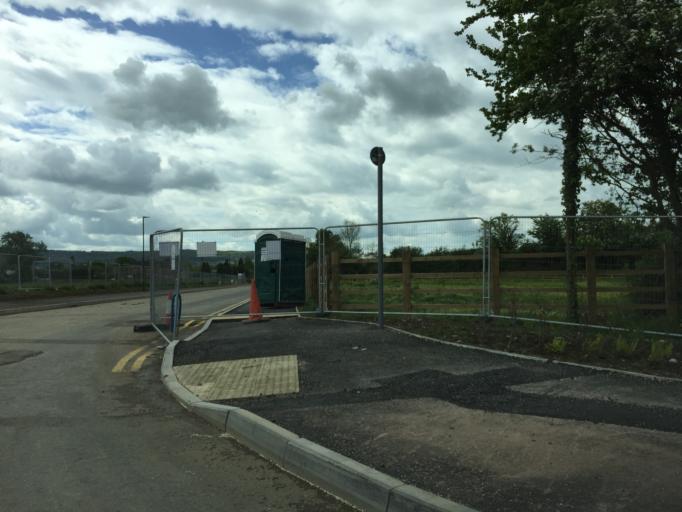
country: GB
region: England
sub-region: Gloucestershire
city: Stonehouse
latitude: 51.7545
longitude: -2.2912
